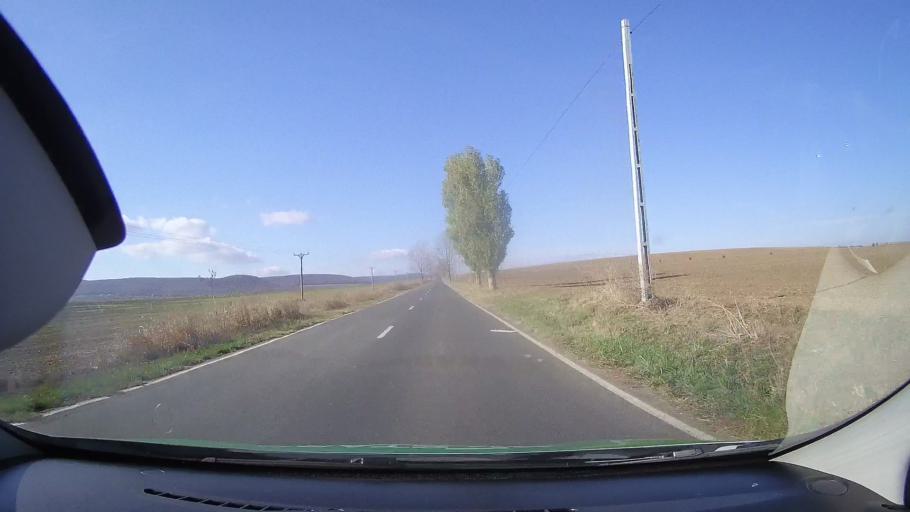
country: RO
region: Tulcea
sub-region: Comuna Sarichioi
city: Enisala
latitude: 44.8789
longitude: 28.7950
